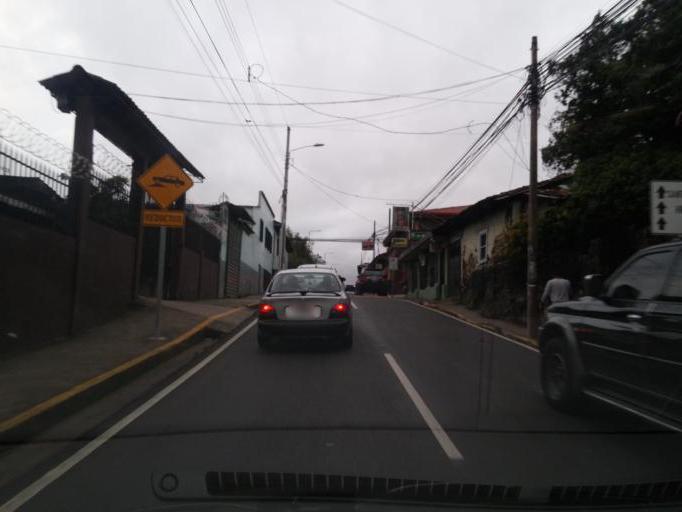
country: CR
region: Heredia
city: Mercedes
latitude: 10.0218
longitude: -84.1247
